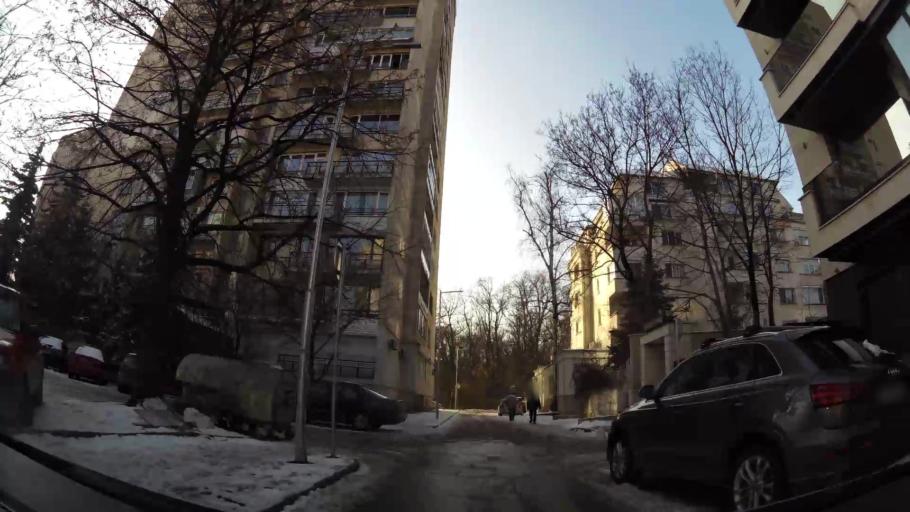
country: BG
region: Sofia-Capital
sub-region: Stolichna Obshtina
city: Sofia
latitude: 42.6685
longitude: 23.3444
